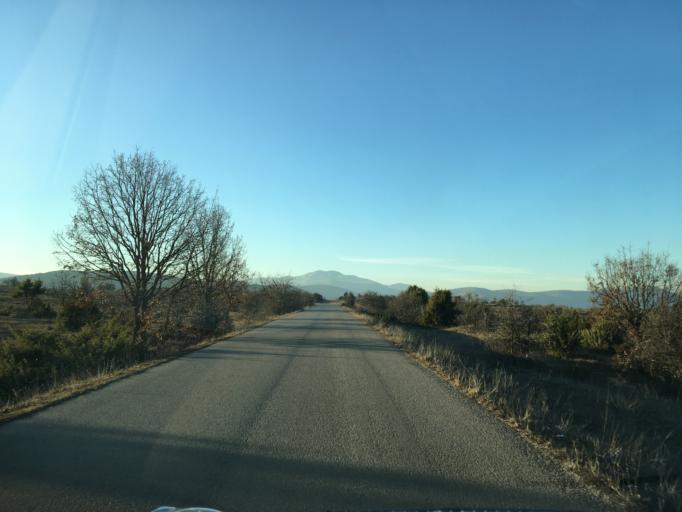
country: GR
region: West Macedonia
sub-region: Nomos Kozanis
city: Kozani
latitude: 40.2737
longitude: 21.7362
